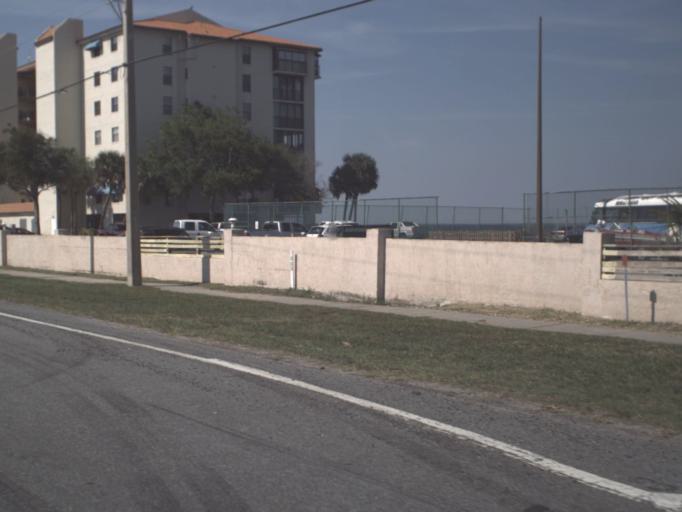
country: US
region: Florida
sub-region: Brevard County
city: Titusville
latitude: 28.5548
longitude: -80.7968
